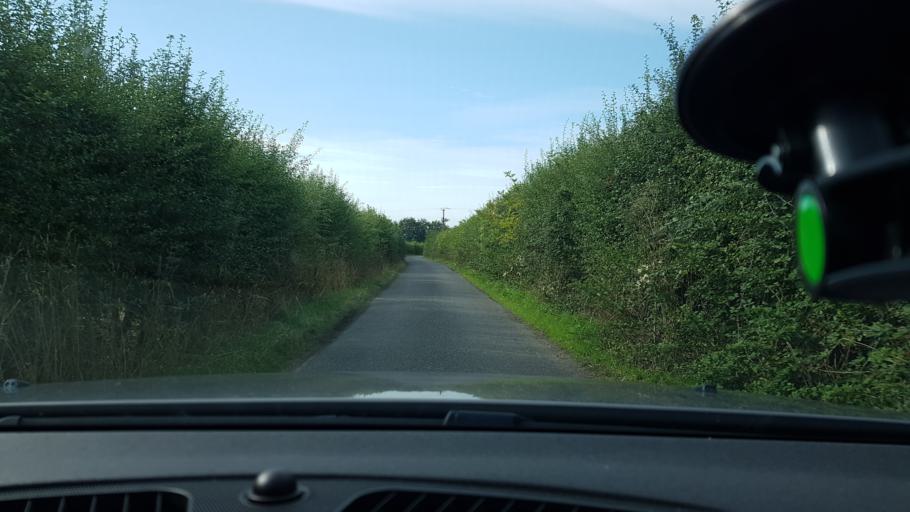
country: GB
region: England
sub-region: West Berkshire
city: Wickham
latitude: 51.4326
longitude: -1.4398
